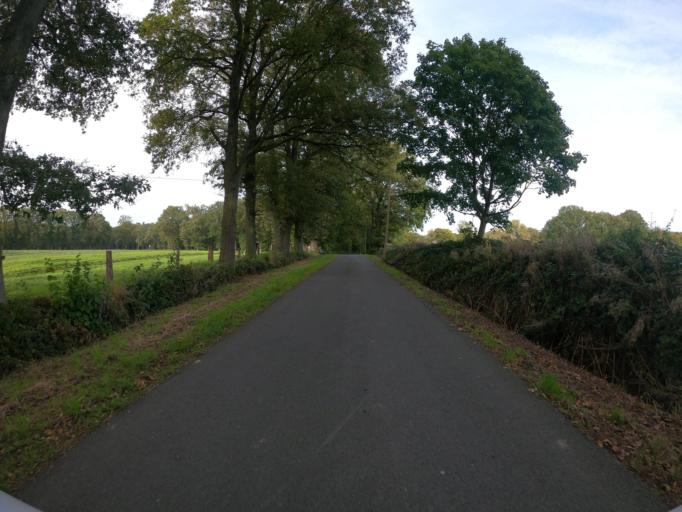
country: DE
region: North Rhine-Westphalia
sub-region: Regierungsbezirk Dusseldorf
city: Schermbeck
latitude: 51.6952
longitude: 6.8579
